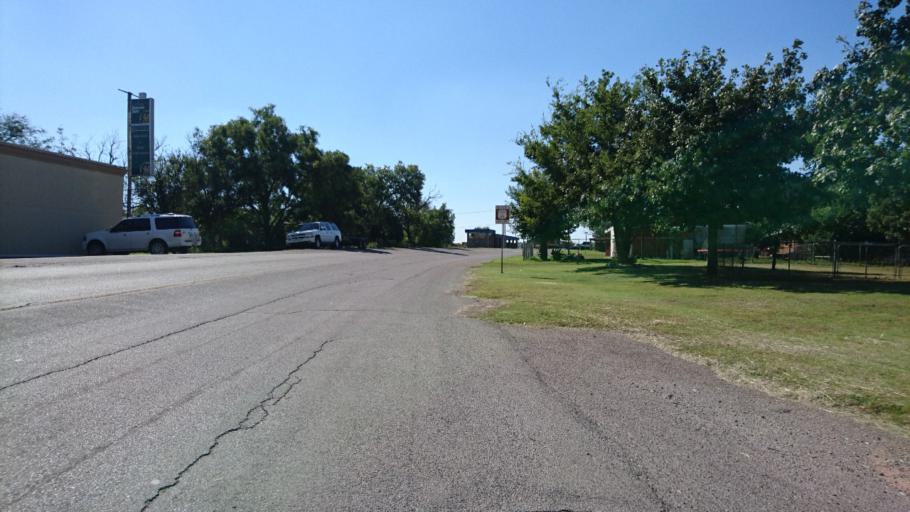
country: US
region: Oklahoma
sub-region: Custer County
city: Clinton
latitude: 35.5068
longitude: -98.9662
